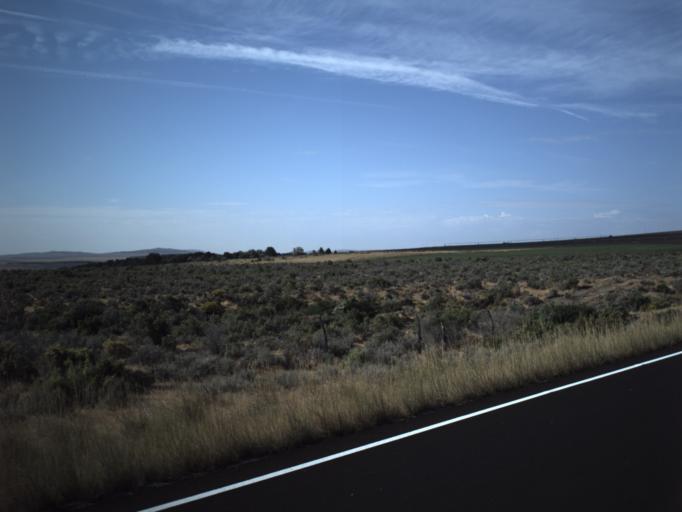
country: US
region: Idaho
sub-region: Minidoka County
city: Heyburn
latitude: 41.8217
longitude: -113.1903
